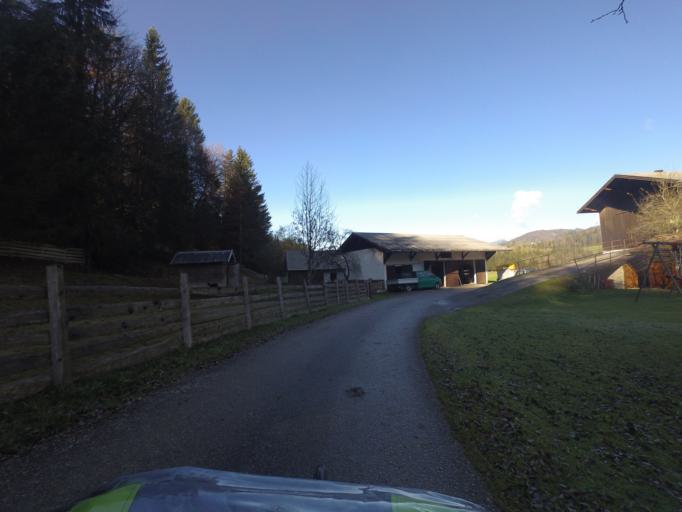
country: AT
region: Salzburg
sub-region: Politischer Bezirk Hallein
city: Adnet
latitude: 47.6772
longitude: 13.1566
